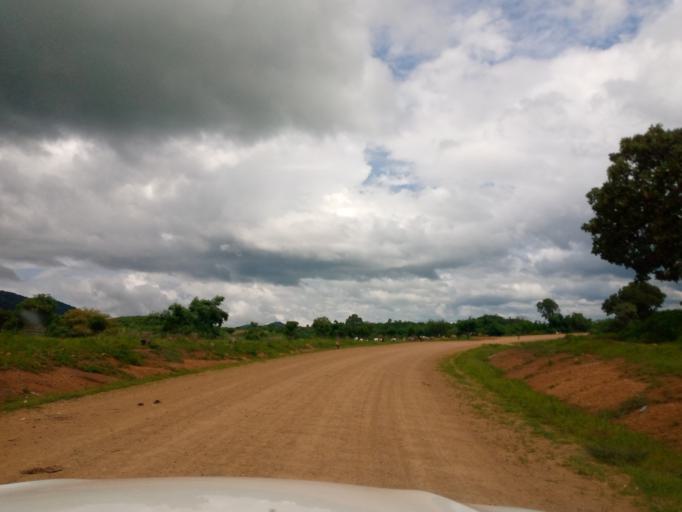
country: ET
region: Oromiya
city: Mendi
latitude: 10.2030
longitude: 35.0926
